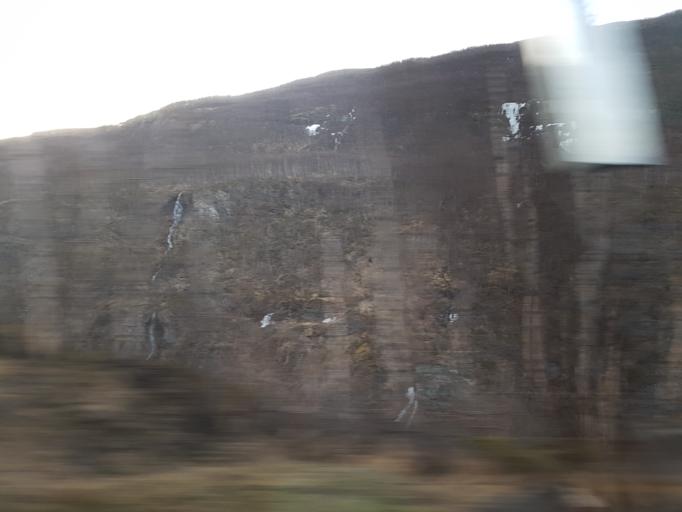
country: NO
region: Sor-Trondelag
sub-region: Oppdal
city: Oppdal
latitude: 62.3525
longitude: 9.6301
